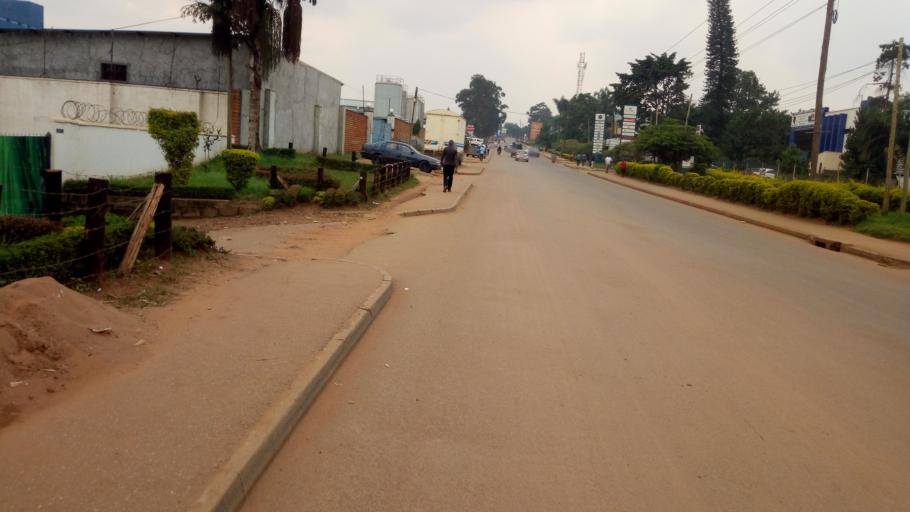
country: UG
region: Central Region
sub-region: Kampala District
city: Kampala
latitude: 0.3169
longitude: 32.6115
